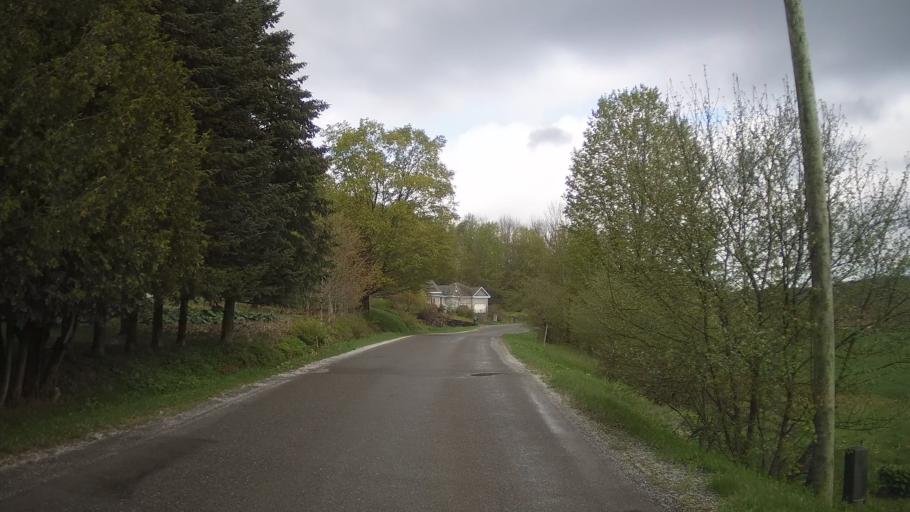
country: CA
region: Quebec
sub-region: Monteregie
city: Cowansville
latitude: 45.1921
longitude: -72.7020
